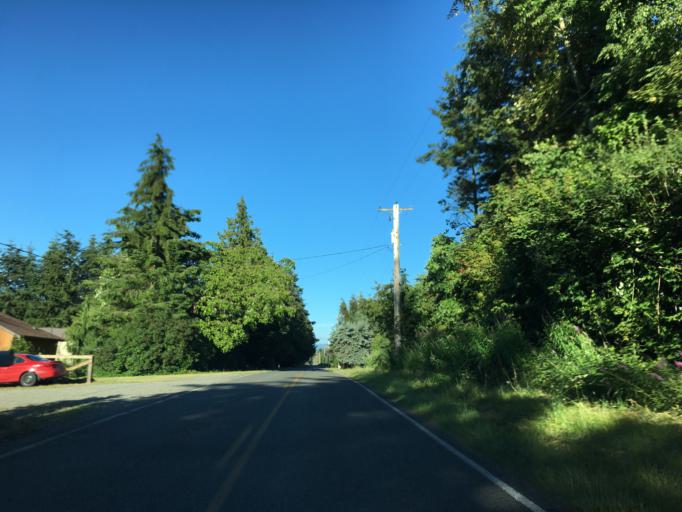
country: US
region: Washington
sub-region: Whatcom County
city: Ferndale
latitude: 48.9135
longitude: -122.6206
